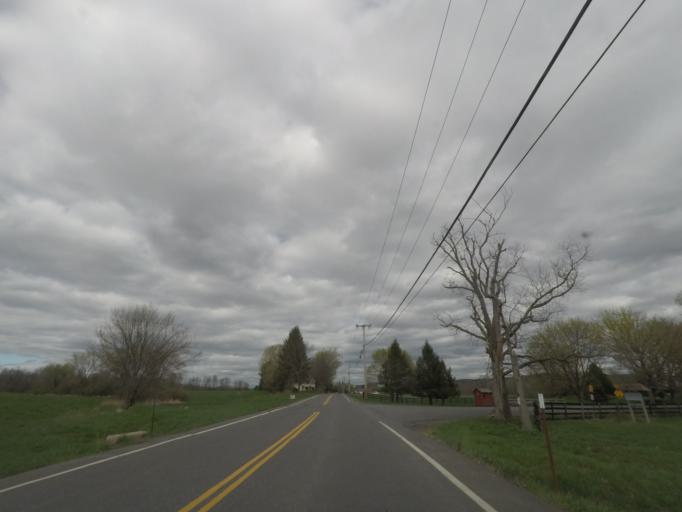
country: US
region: New York
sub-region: Columbia County
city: Philmont
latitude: 42.2835
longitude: -73.6542
